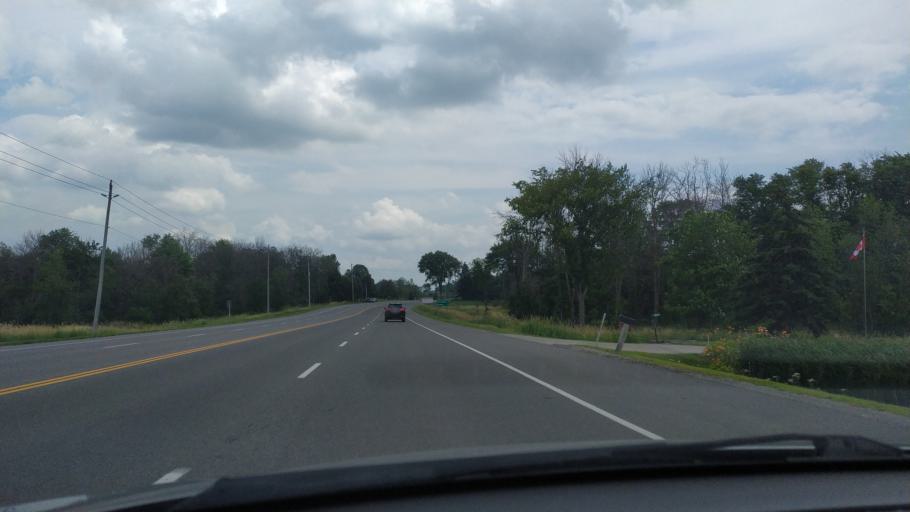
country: CA
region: Ontario
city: Stratford
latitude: 43.3705
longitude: -80.9269
